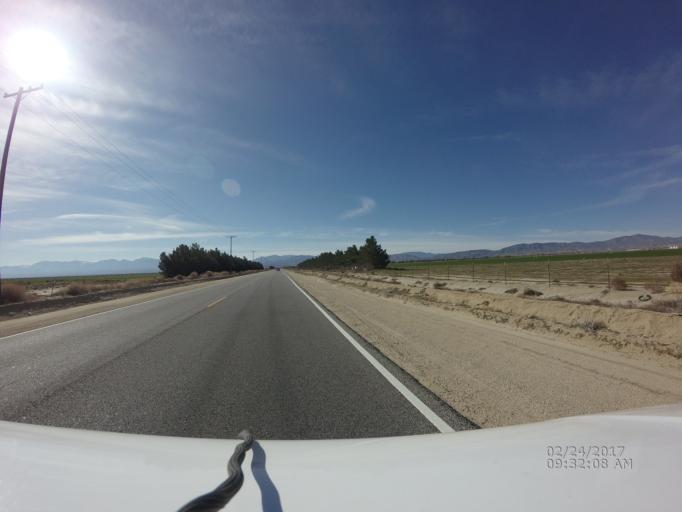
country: US
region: California
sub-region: Los Angeles County
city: Palmdale
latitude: 34.6150
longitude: -118.0410
